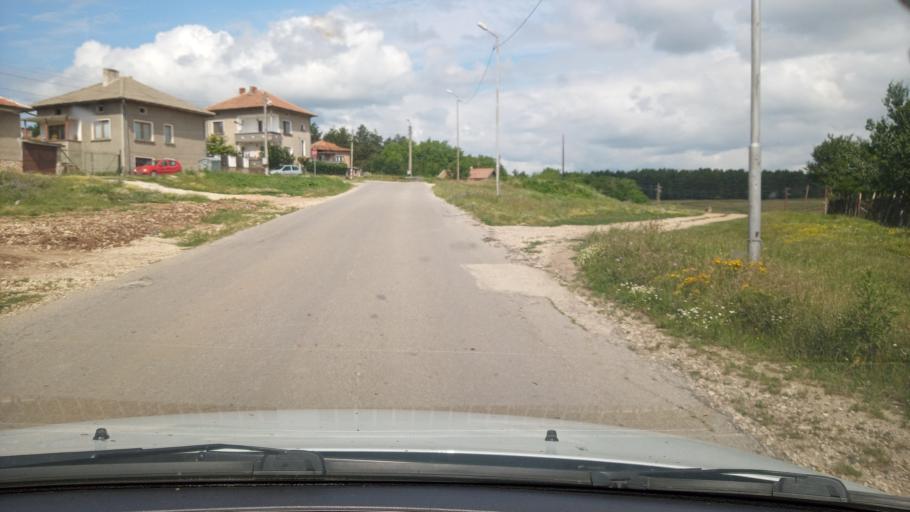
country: BG
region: Lovech
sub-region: Obshtina Lukovit
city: Lukovit
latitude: 43.2075
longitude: 24.1533
